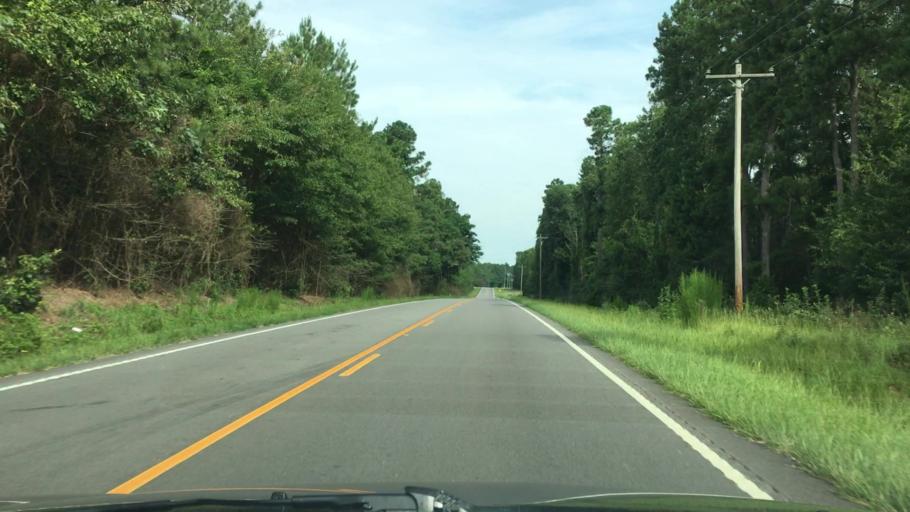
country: US
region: South Carolina
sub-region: Lexington County
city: Batesburg-Leesville
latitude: 33.7074
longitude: -81.4893
